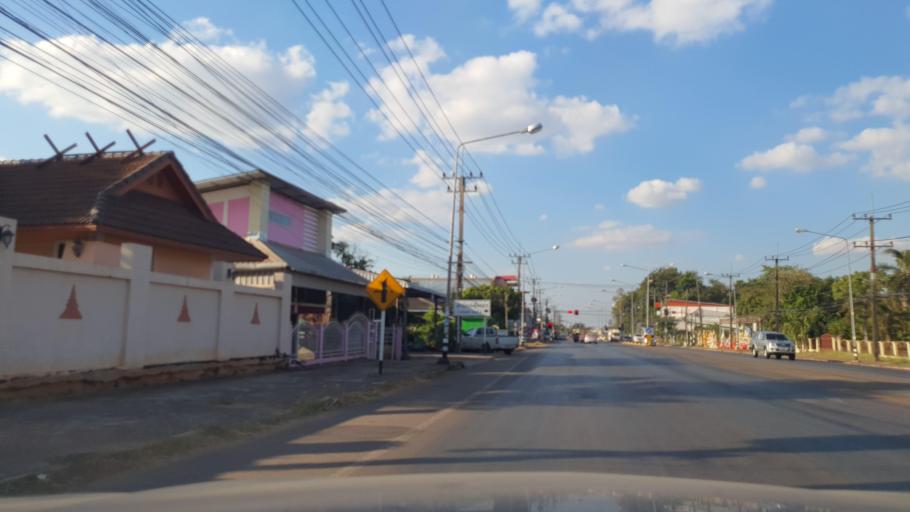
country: TH
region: Sakon Nakhon
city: Sakon Nakhon
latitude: 17.1822
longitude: 104.0944
